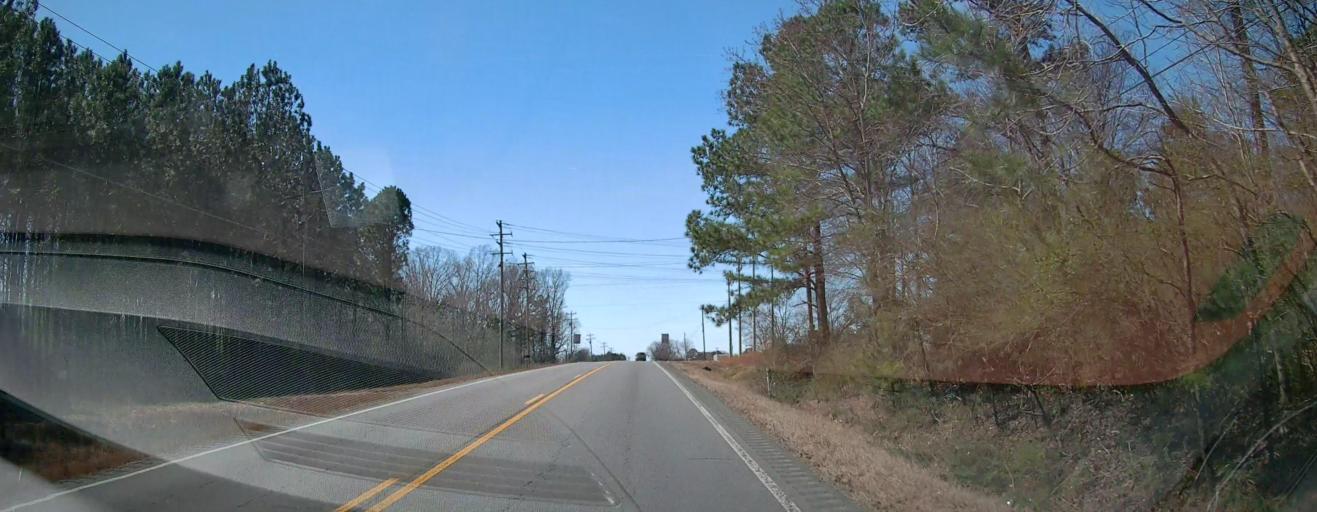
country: US
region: Alabama
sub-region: Blount County
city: Blountsville
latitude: 34.1747
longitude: -86.6361
